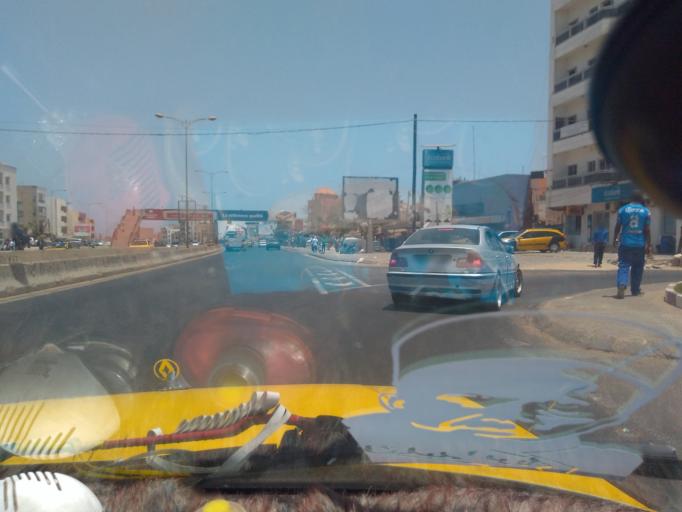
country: SN
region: Dakar
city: Grand Dakar
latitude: 14.7543
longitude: -17.4680
